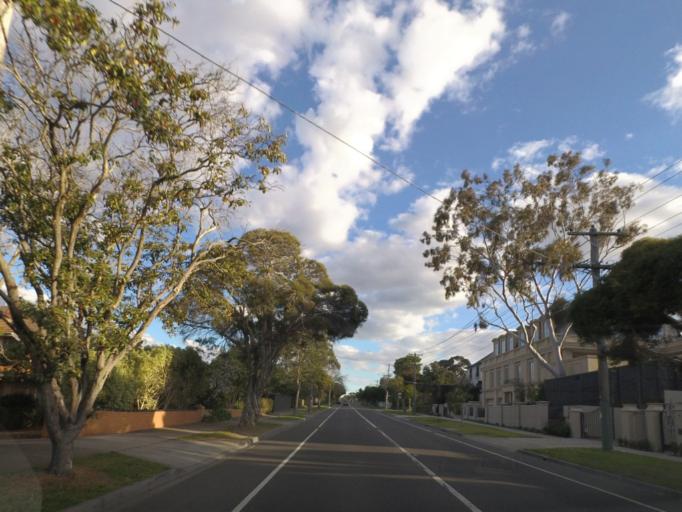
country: AU
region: Victoria
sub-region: Boroondara
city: Balwyn North
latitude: -37.7986
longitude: 145.0981
